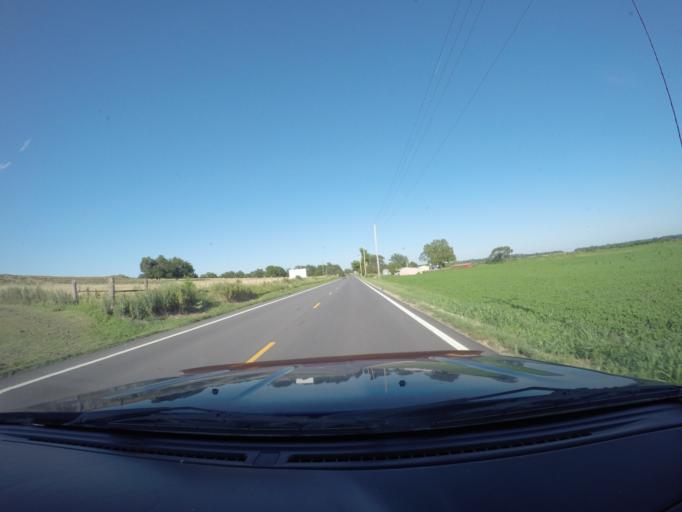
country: US
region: Kansas
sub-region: Douglas County
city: Lawrence
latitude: 39.0657
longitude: -95.3110
